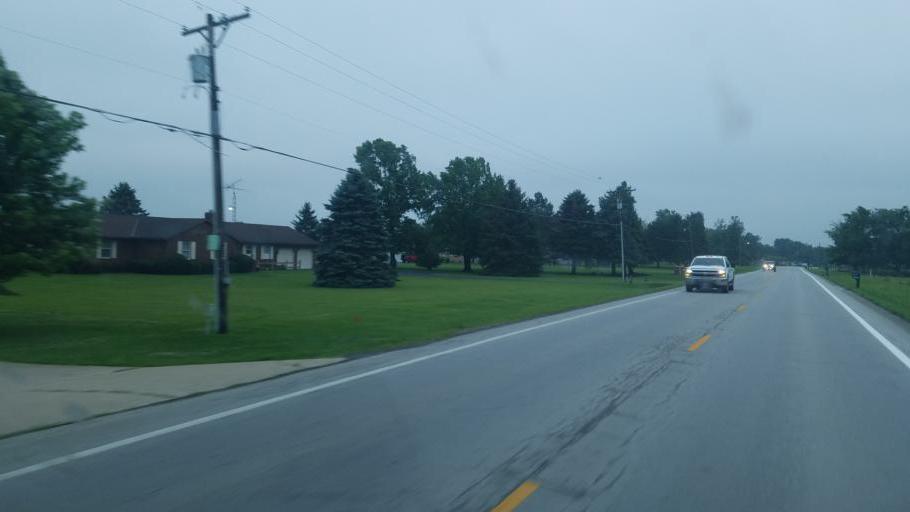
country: US
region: Ohio
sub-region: Fayette County
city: Washington Court House
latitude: 39.5730
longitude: -83.4001
